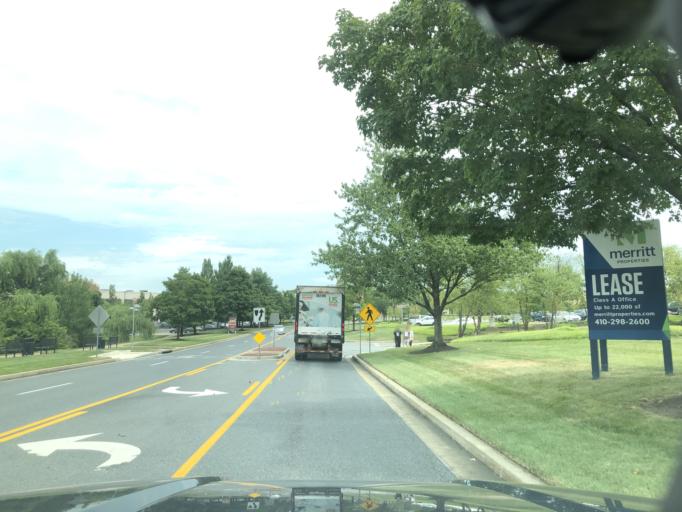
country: US
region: Maryland
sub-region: Howard County
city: Savage
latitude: 39.1895
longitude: -76.8172
